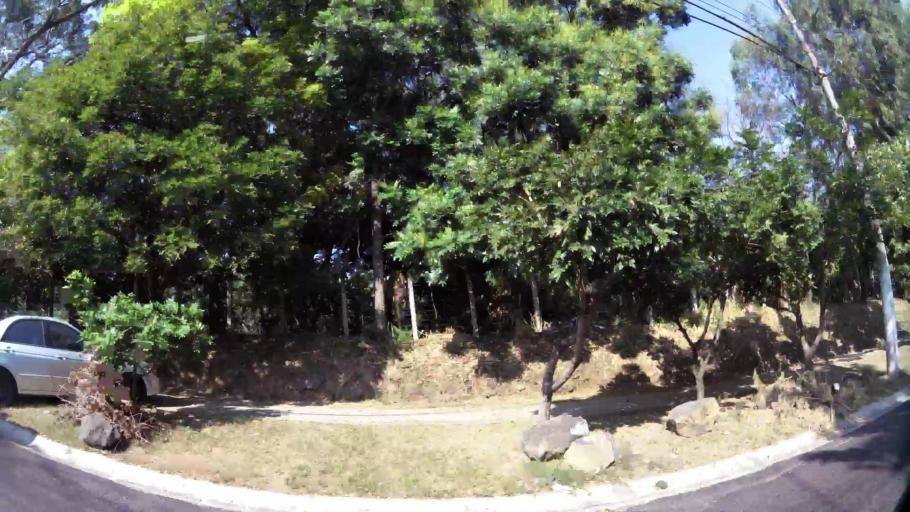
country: SV
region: La Libertad
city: Antiguo Cuscatlan
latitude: 13.6788
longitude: -89.2342
